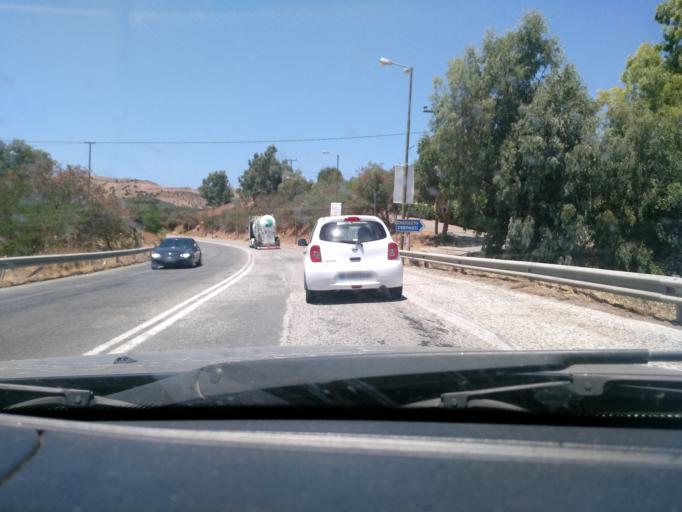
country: GR
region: Crete
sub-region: Nomos Rethymnis
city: Panormos
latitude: 35.4122
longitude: 24.7219
